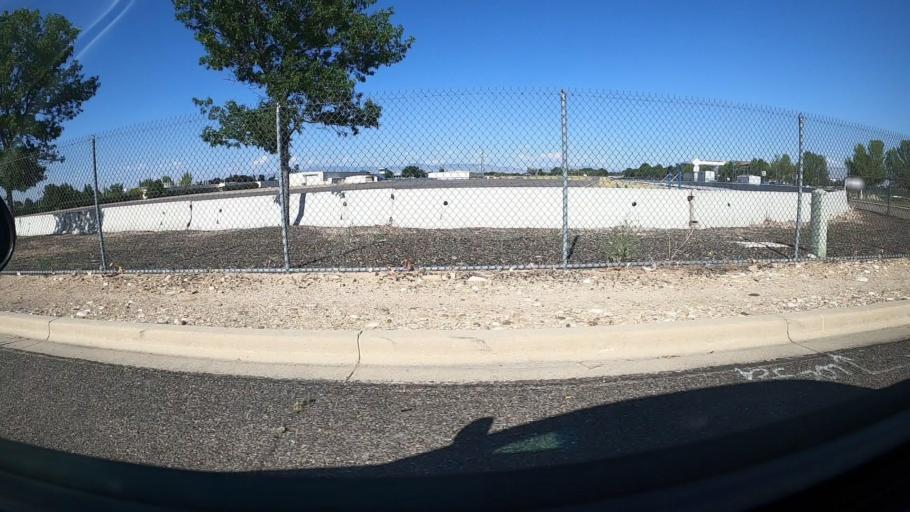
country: US
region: Idaho
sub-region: Ada County
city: Meridian
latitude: 43.5965
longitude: -116.3845
